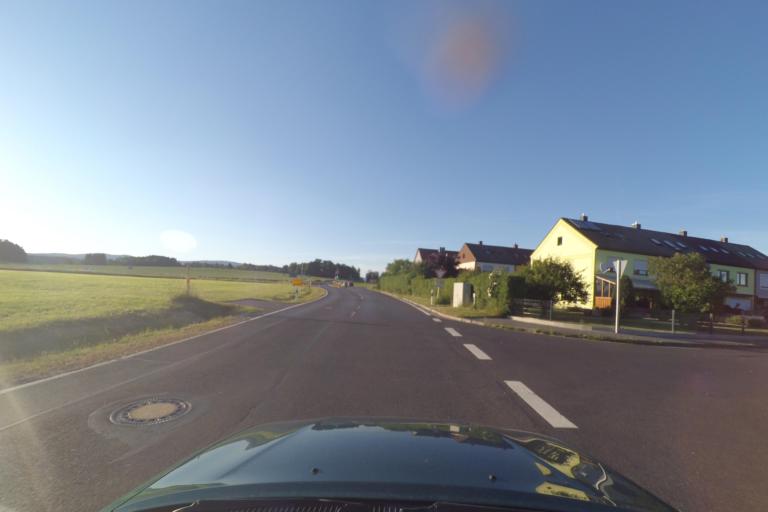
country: DE
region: Bavaria
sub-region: Upper Palatinate
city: Krummennaab
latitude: 49.8340
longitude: 12.1043
